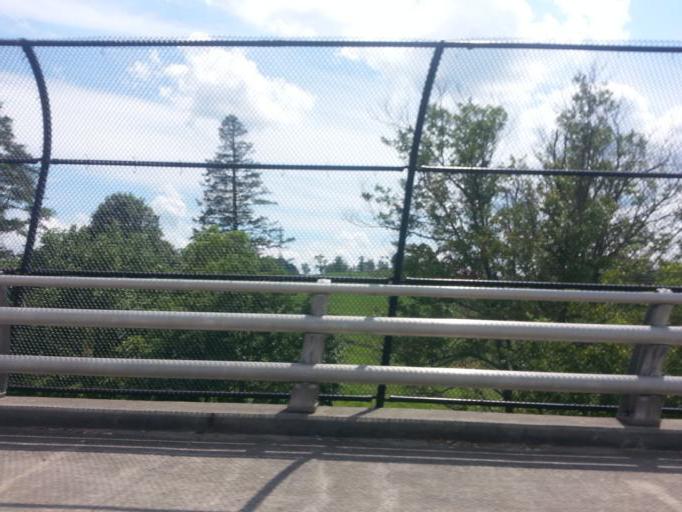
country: US
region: Virginia
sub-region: Washington County
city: Abingdon
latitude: 36.7181
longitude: -81.9503
